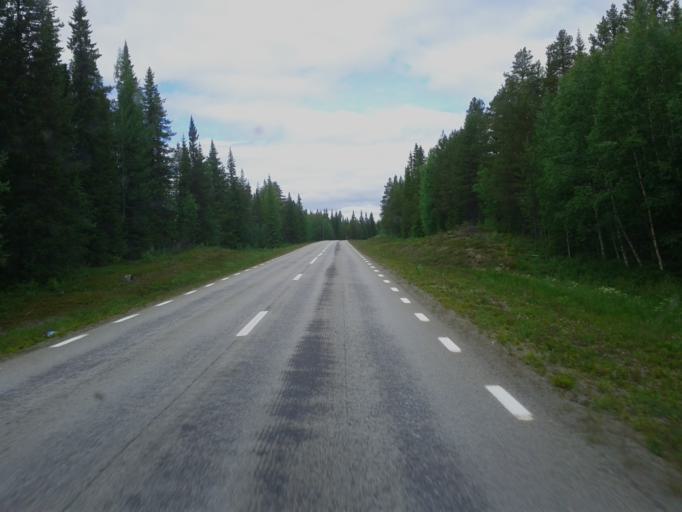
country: SE
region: Vaesterbotten
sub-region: Storumans Kommun
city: Fristad
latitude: 65.3654
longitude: 16.5254
